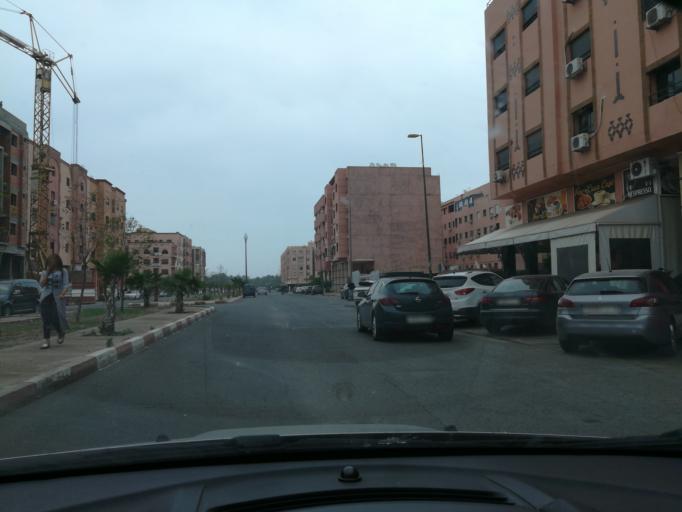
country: MA
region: Marrakech-Tensift-Al Haouz
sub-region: Marrakech
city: Marrakesh
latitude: 31.6760
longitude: -8.0264
